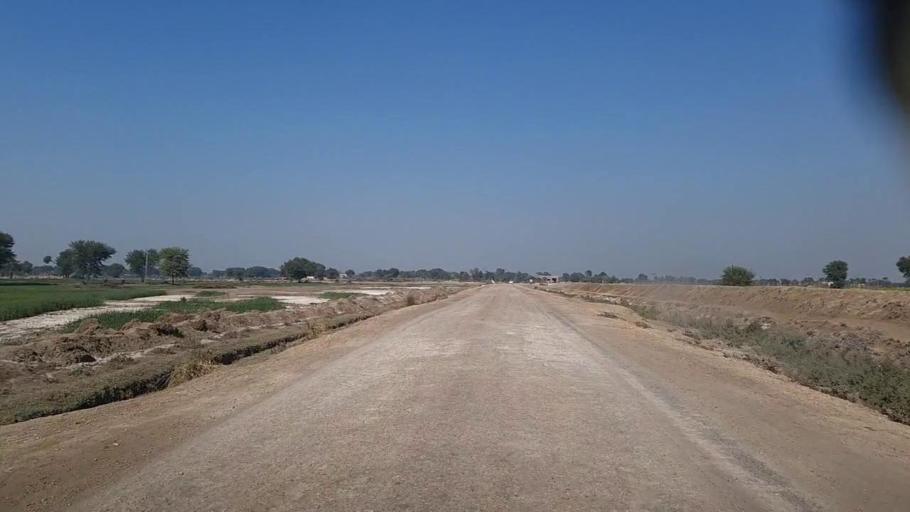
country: PK
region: Sindh
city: Khairpur
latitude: 27.9899
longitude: 69.8478
